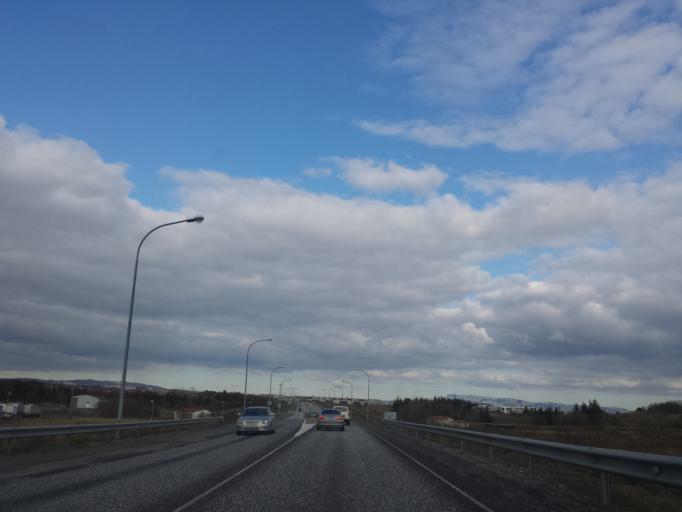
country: IS
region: Capital Region
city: Reykjavik
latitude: 64.0971
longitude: -21.7976
